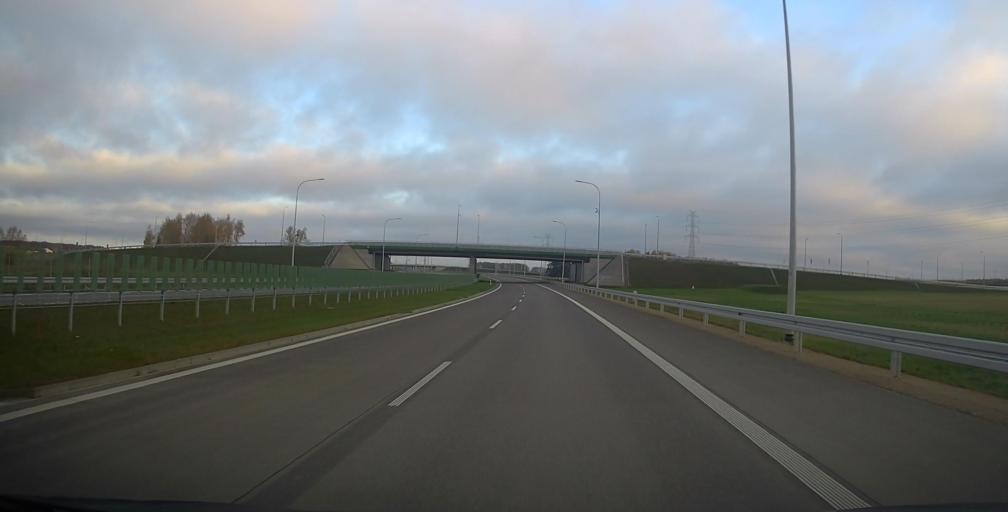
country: PL
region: Podlasie
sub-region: Powiat grajewski
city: Szczuczyn
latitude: 53.5885
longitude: 22.3280
